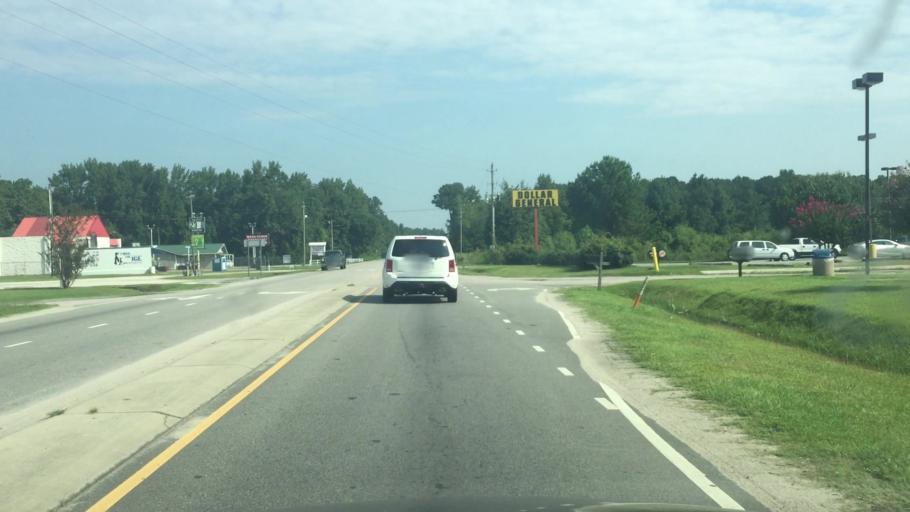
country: US
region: North Carolina
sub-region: Columbus County
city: Chadbourn
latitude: 34.3324
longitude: -78.8265
